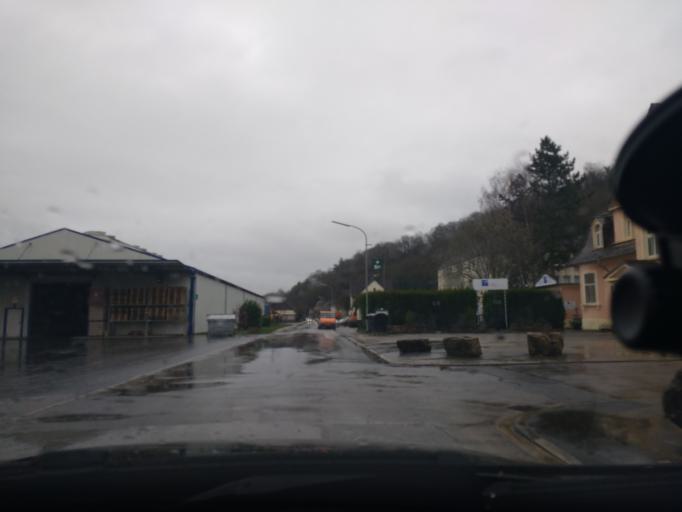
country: LU
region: Grevenmacher
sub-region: Canton de Grevenmacher
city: Grevenmacher
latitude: 49.6712
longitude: 6.4397
